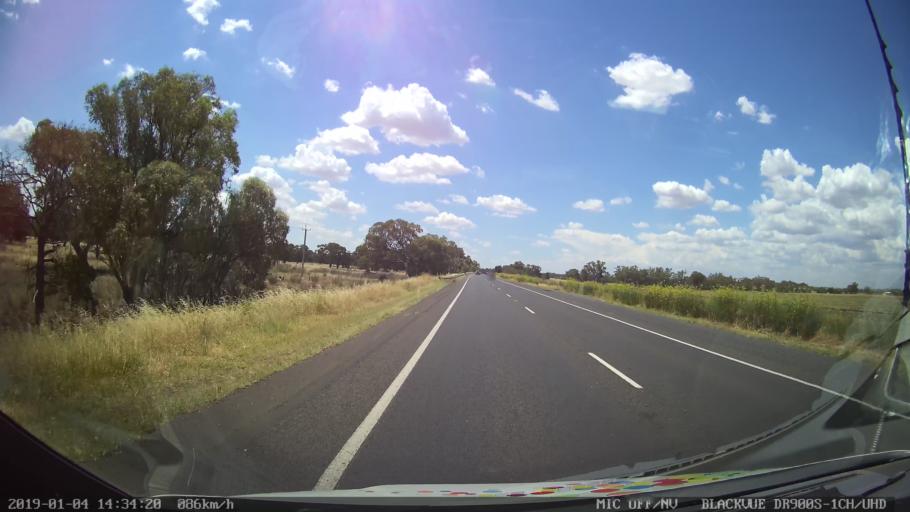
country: AU
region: New South Wales
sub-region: Dubbo Municipality
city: Dubbo
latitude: -32.1999
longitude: 148.6201
